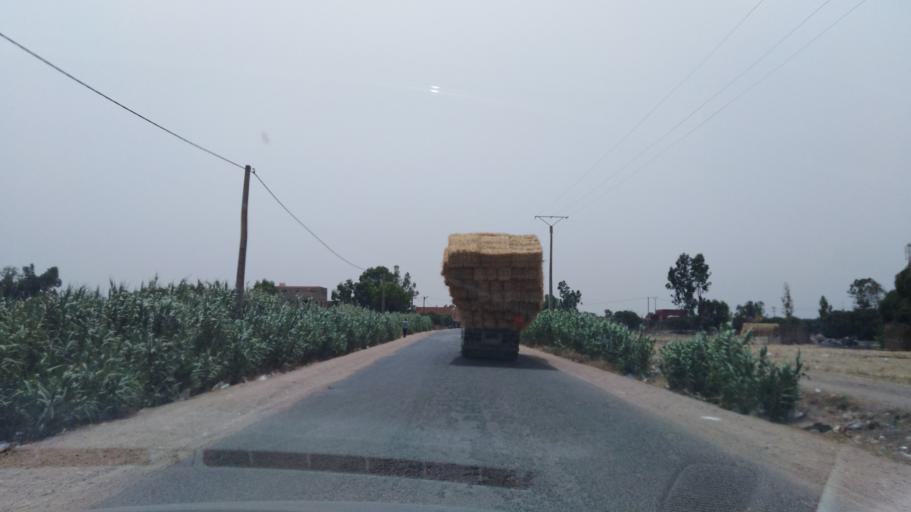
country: MA
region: Grand Casablanca
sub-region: Mediouna
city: Mediouna
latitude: 33.4019
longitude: -7.5127
